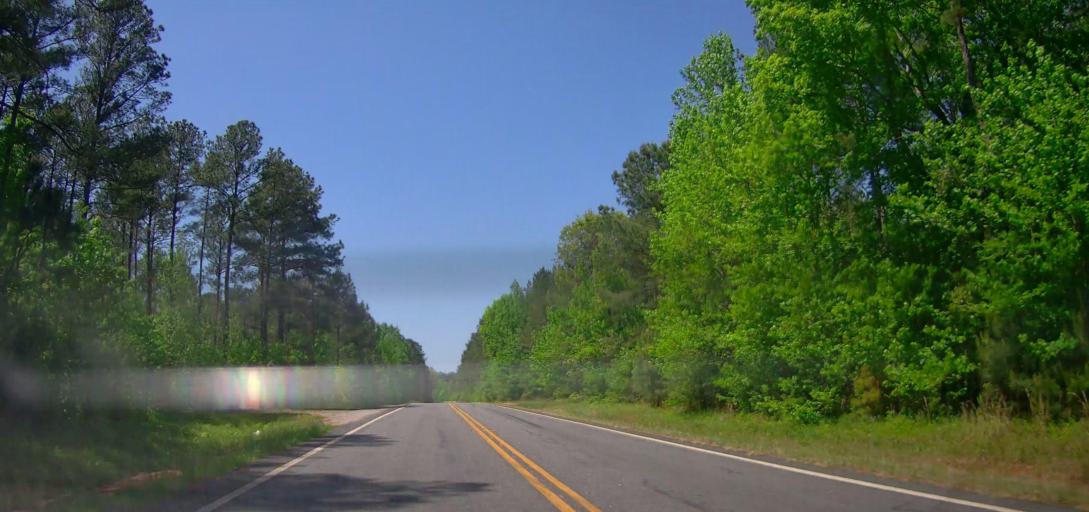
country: US
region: Georgia
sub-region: Putnam County
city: Eatonton
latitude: 33.2147
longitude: -83.4840
